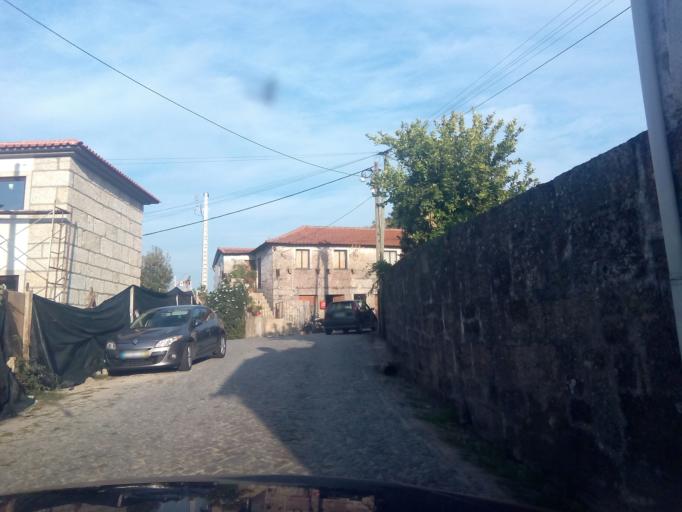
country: PT
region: Porto
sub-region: Lousada
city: Meinedo
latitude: 41.2279
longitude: -8.2055
